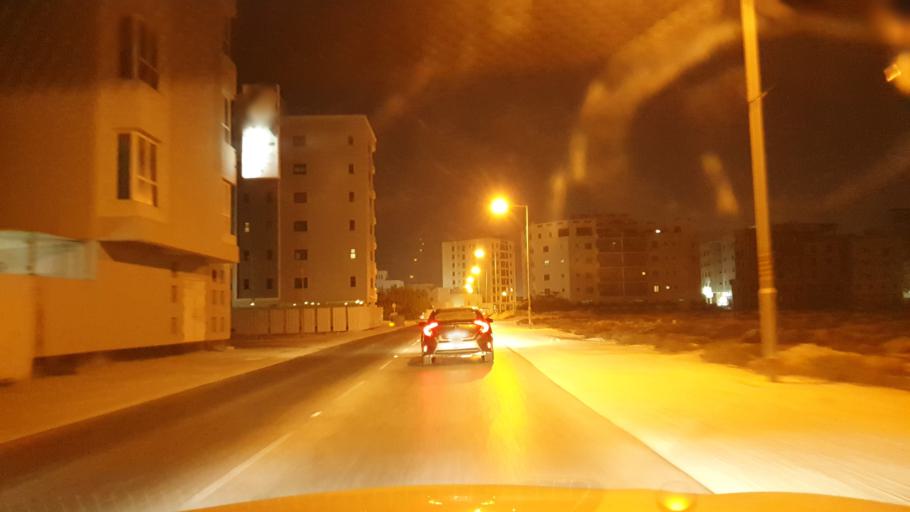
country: BH
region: Northern
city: Madinat `Isa
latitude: 26.1883
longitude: 50.4820
